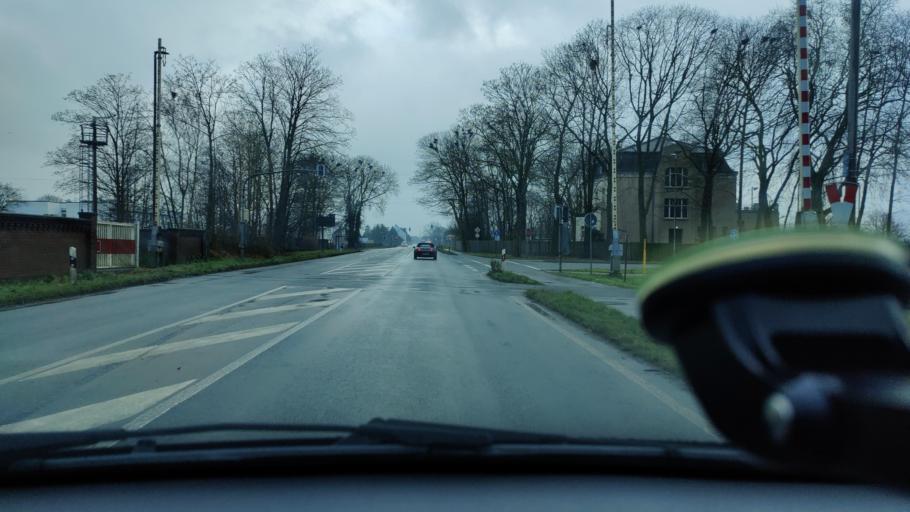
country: DE
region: North Rhine-Westphalia
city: Rheinberg
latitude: 51.5606
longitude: 6.5831
